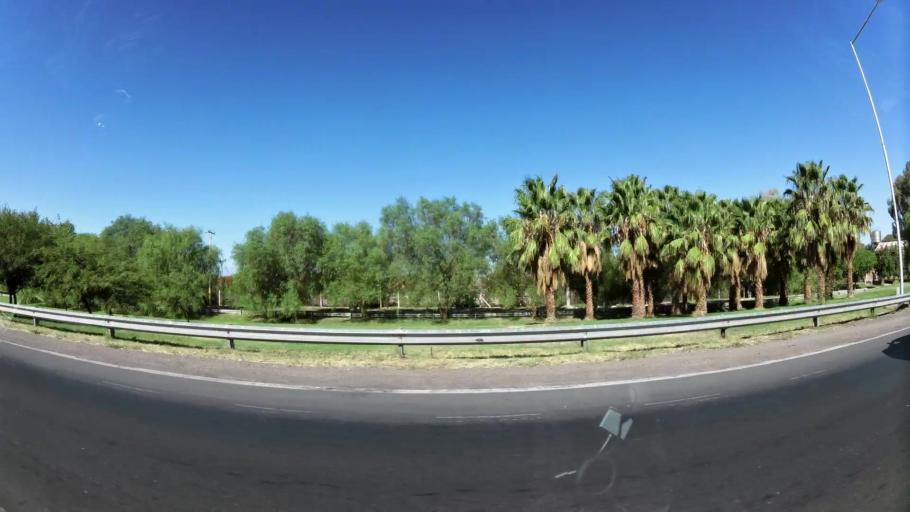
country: AR
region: San Juan
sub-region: Departamento de Santa Lucia
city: Santa Lucia
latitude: -31.5282
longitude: -68.5035
